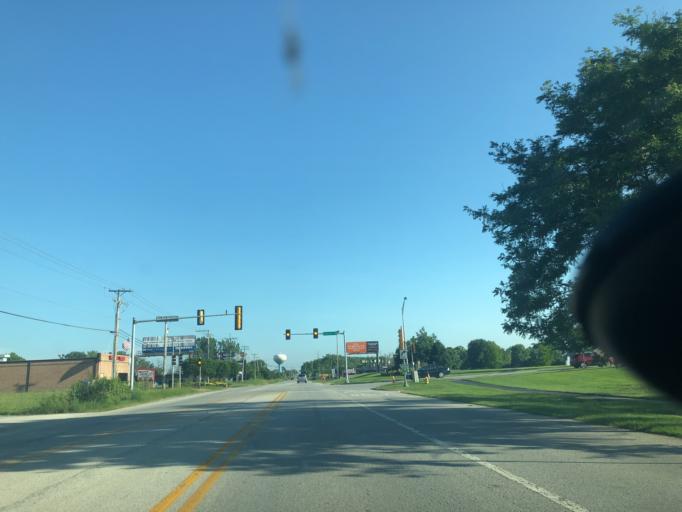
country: US
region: Illinois
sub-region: Cook County
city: Orland Hills
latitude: 41.5774
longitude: -87.8908
